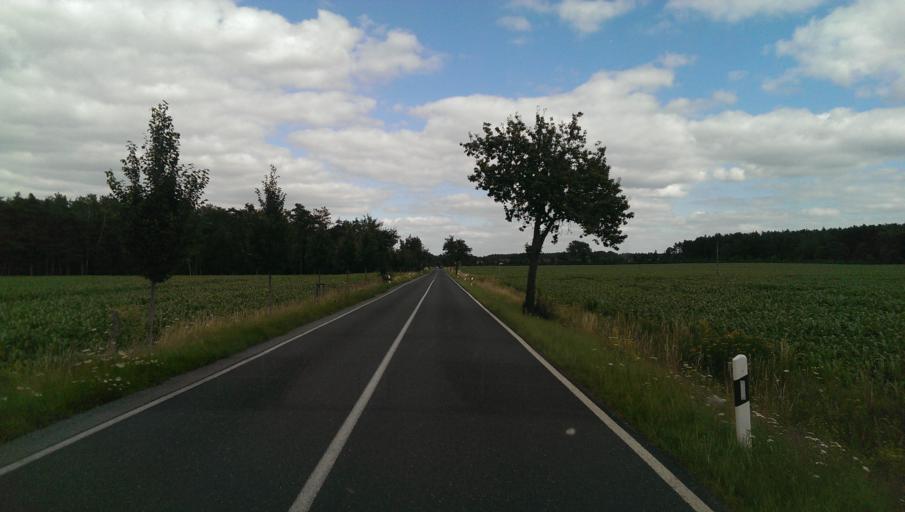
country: DE
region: Saxony-Anhalt
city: Radis
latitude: 51.7866
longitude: 12.4759
